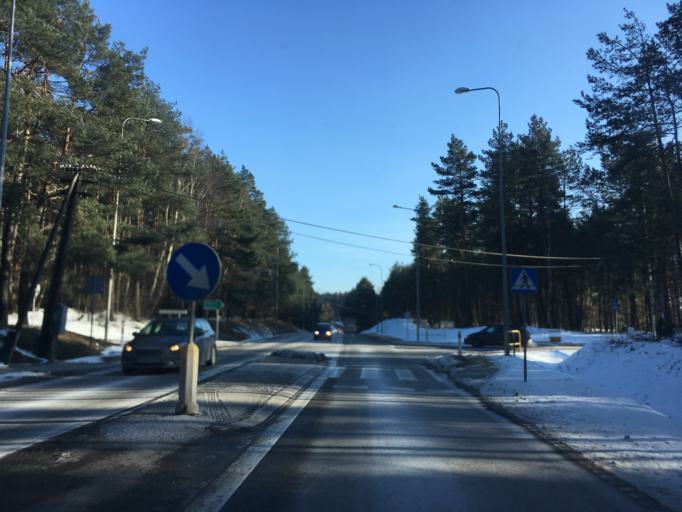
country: PL
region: Pomeranian Voivodeship
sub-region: Powiat koscierski
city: Koscierzyna
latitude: 54.1209
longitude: 17.8851
